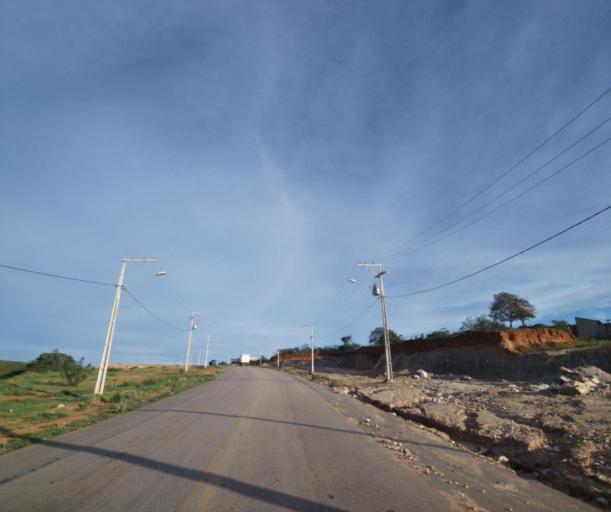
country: BR
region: Bahia
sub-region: Cacule
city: Cacule
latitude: -14.2081
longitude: -42.1075
